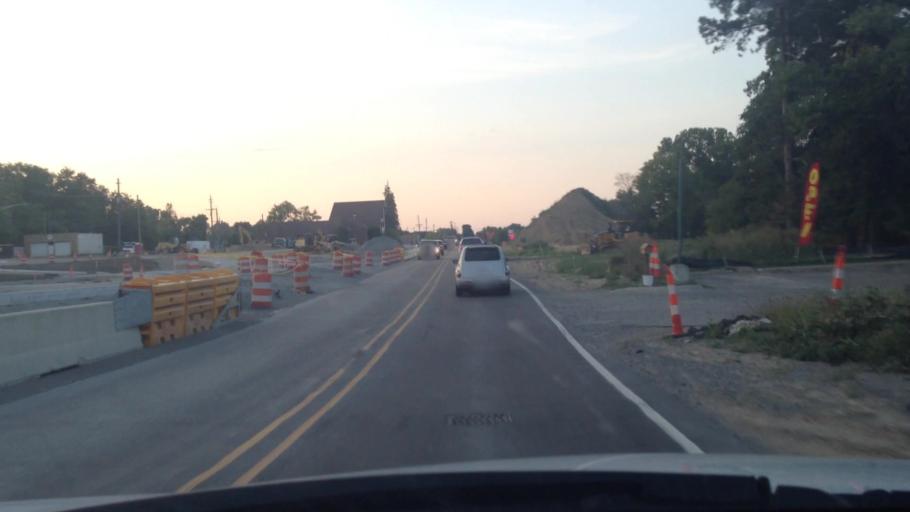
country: US
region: Michigan
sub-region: Oakland County
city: Auburn Hills
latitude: 42.7202
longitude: -83.3073
